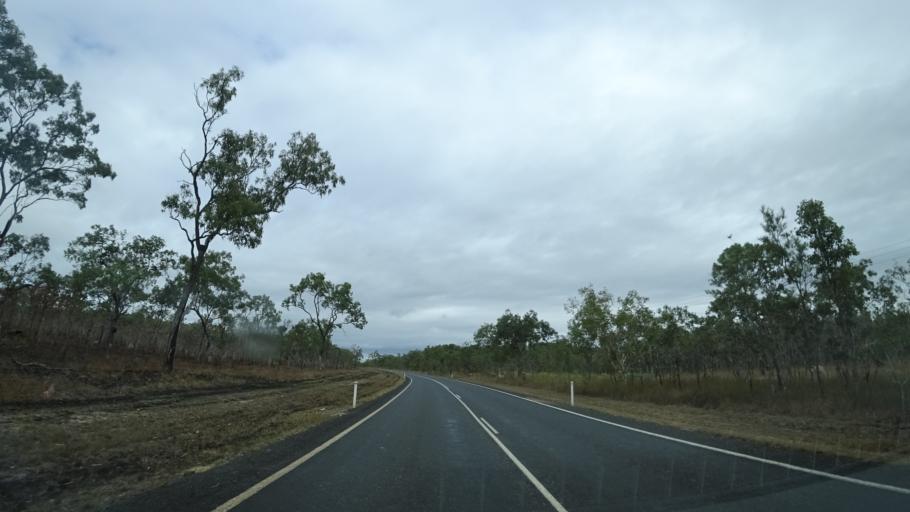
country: AU
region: Queensland
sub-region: Tablelands
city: Mareeba
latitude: -16.7731
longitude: 145.3401
